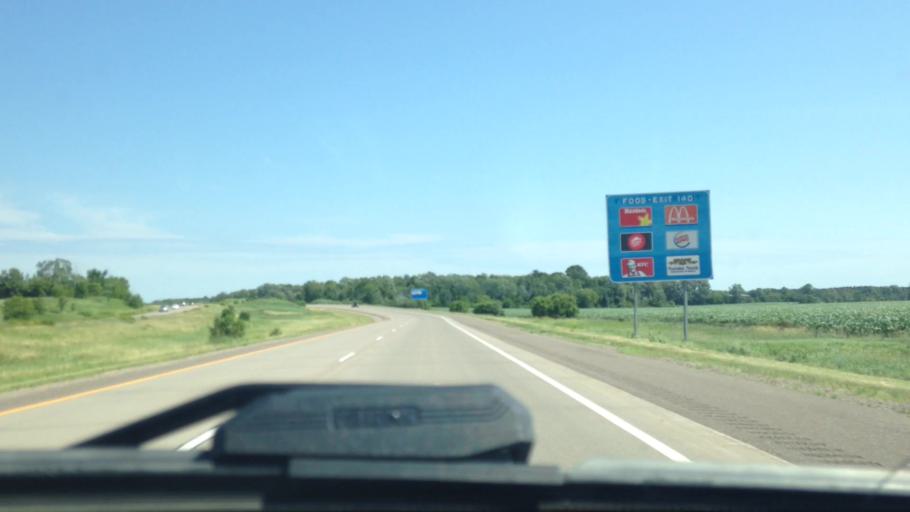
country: US
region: Wisconsin
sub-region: Barron County
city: Rice Lake
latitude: 45.4622
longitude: -91.7579
